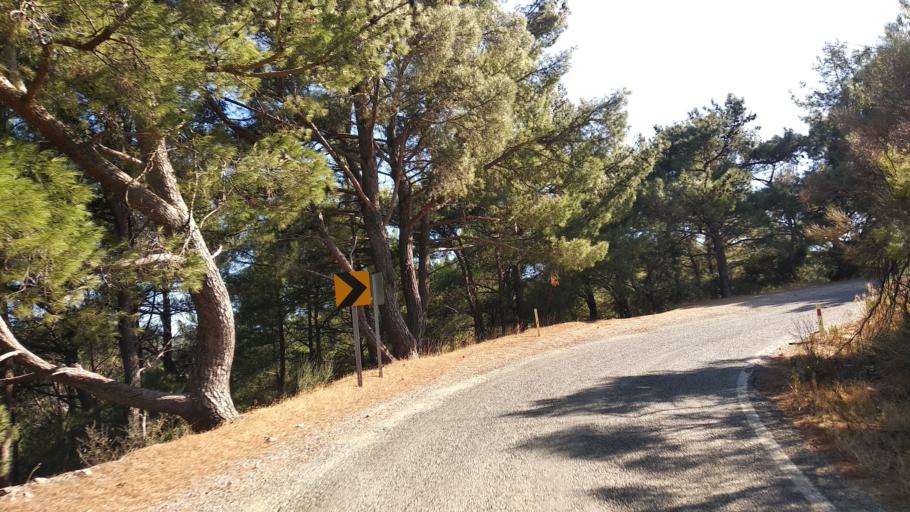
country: TR
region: Izmir
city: Gaziemir
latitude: 38.3261
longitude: 26.9559
